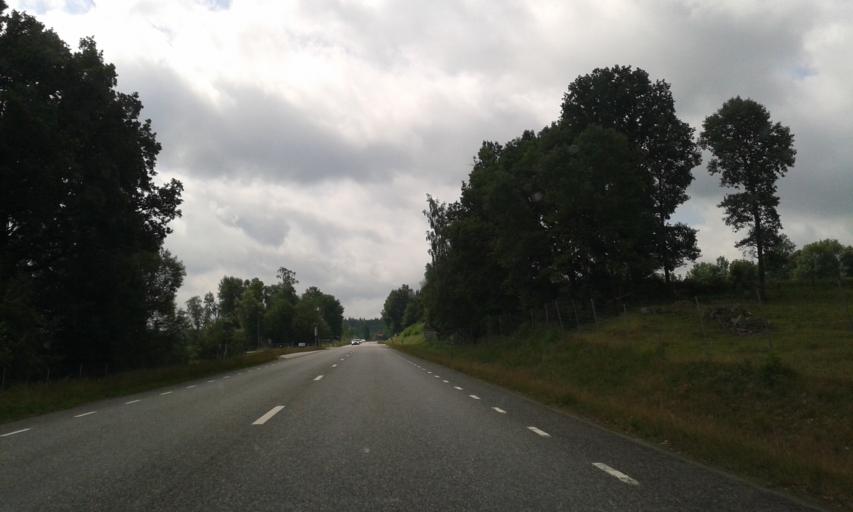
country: SE
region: Vaestra Goetaland
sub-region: Tranemo Kommun
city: Limmared
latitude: 57.5228
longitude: 13.3417
